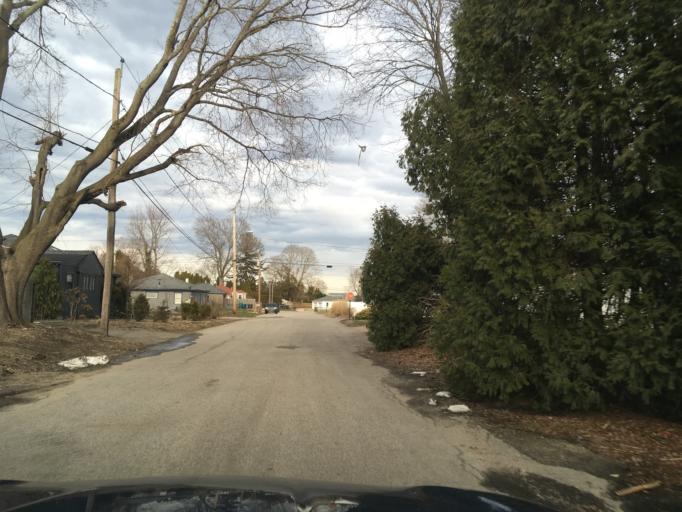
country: US
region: Rhode Island
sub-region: Kent County
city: East Greenwich
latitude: 41.6658
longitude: -71.4232
